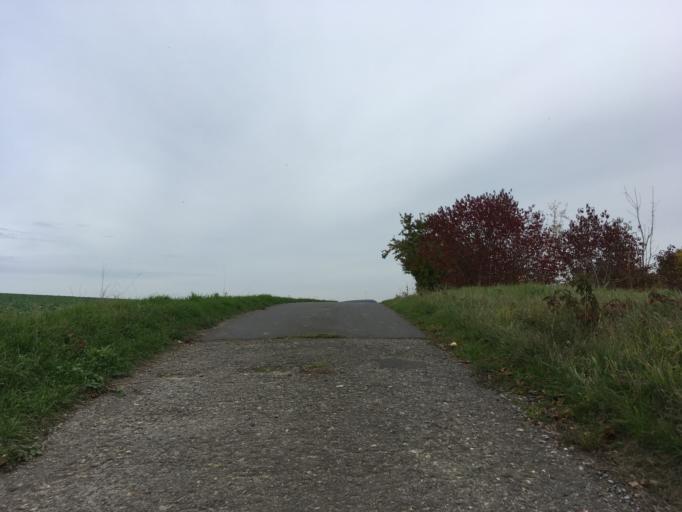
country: DE
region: Baden-Wuerttemberg
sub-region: Karlsruhe Region
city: Buchen
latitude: 49.5054
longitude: 9.3105
